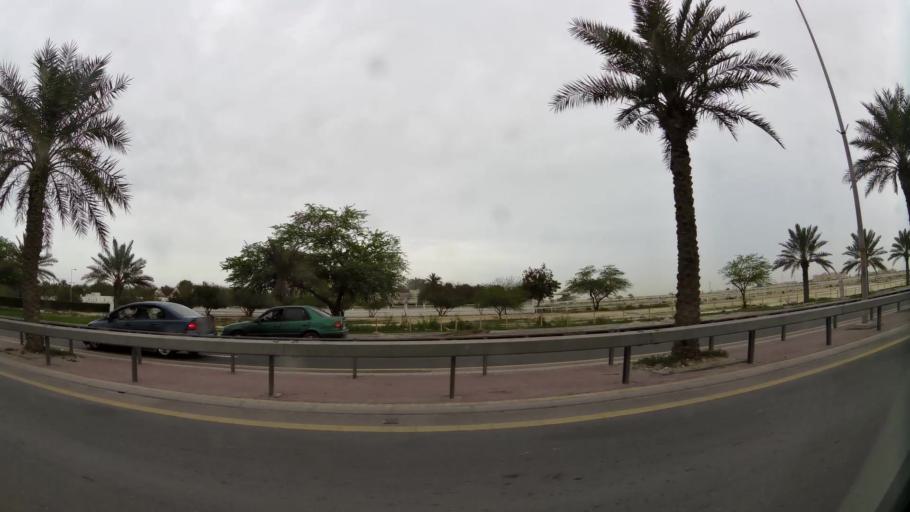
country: BH
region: Northern
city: Ar Rifa'
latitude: 26.1072
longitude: 50.5399
